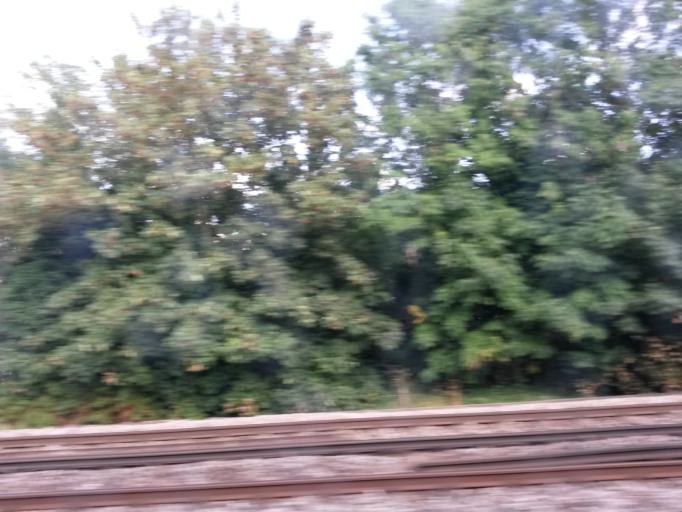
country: GB
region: England
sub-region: Greater London
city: Catford
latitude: 51.4410
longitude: -0.0524
